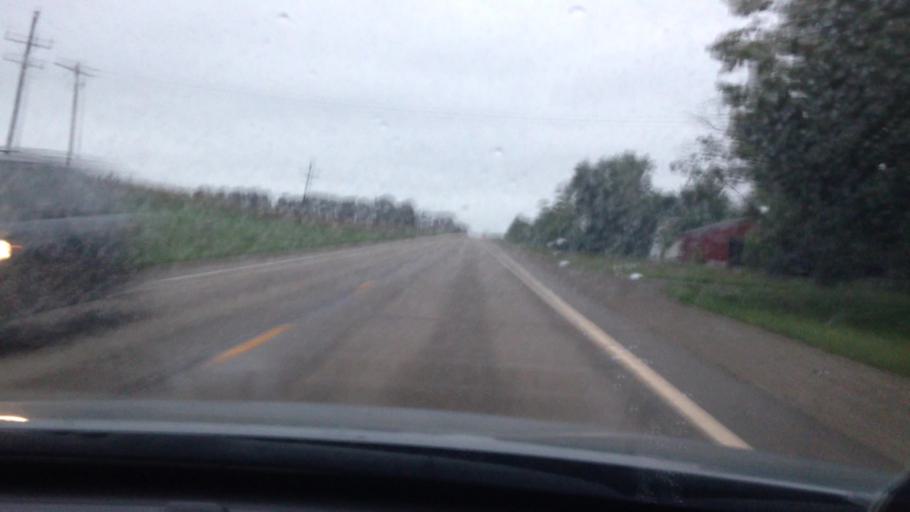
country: US
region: Kansas
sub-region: Brown County
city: Hiawatha
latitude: 39.8236
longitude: -95.5271
